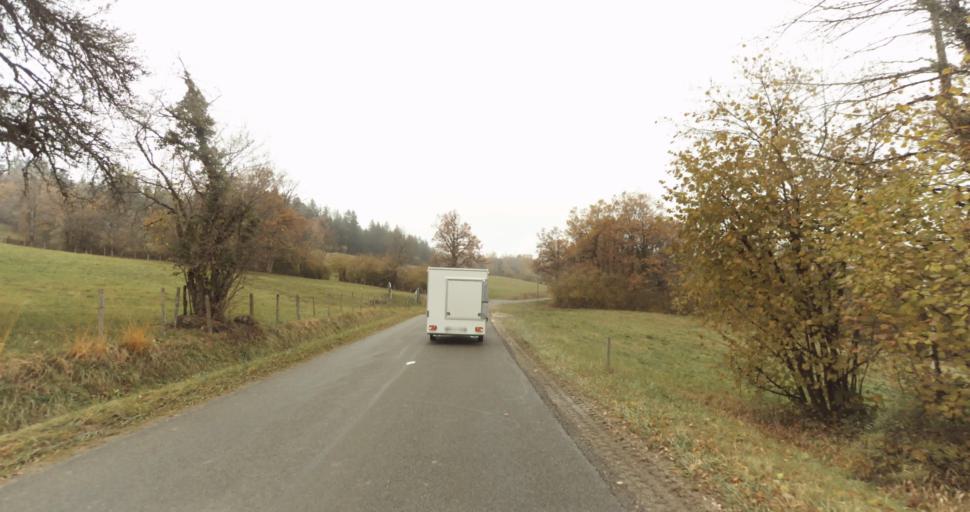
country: FR
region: Rhone-Alpes
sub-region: Departement de la Haute-Savoie
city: Groisy
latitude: 46.0205
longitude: 6.1780
